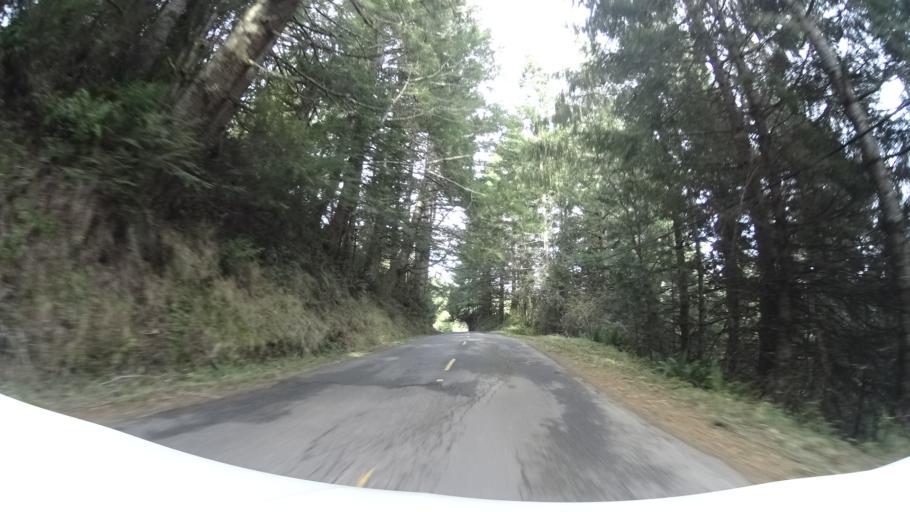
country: US
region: California
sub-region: Humboldt County
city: Ferndale
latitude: 40.5288
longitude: -124.2690
